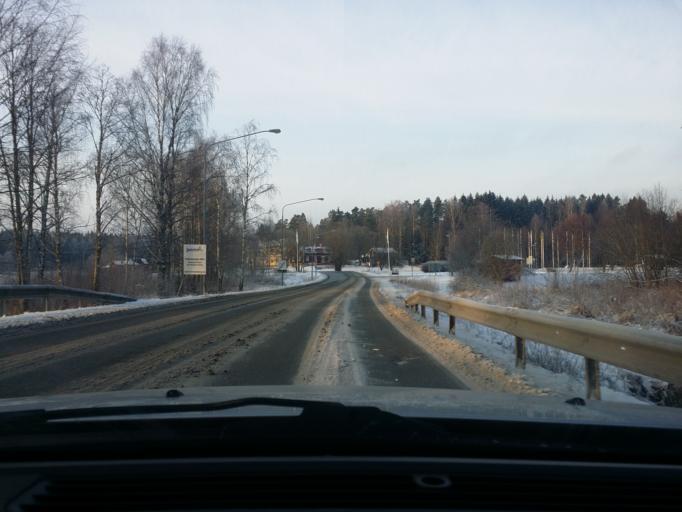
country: SE
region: OErebro
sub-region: Lindesbergs Kommun
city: Lindesberg
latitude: 59.6013
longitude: 15.1884
